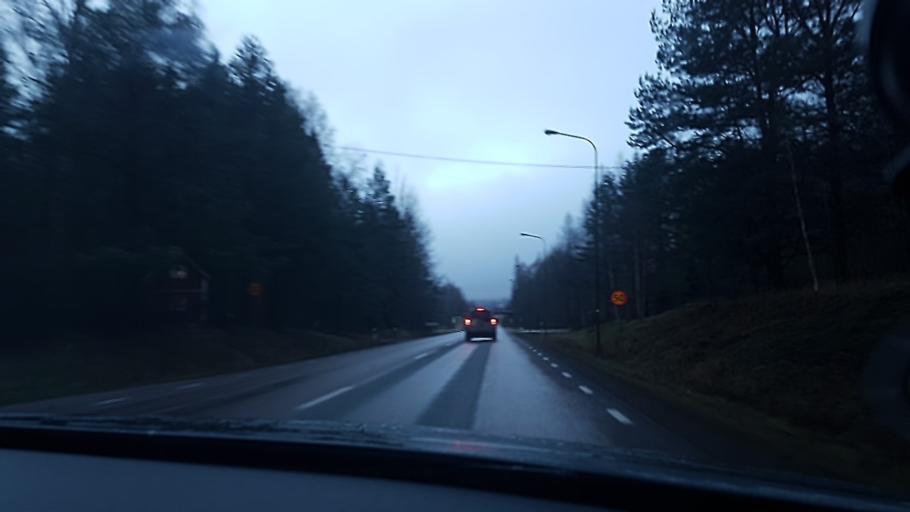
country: SE
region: Vaermland
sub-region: Kristinehamns Kommun
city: Kristinehamn
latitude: 59.3276
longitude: 14.1168
